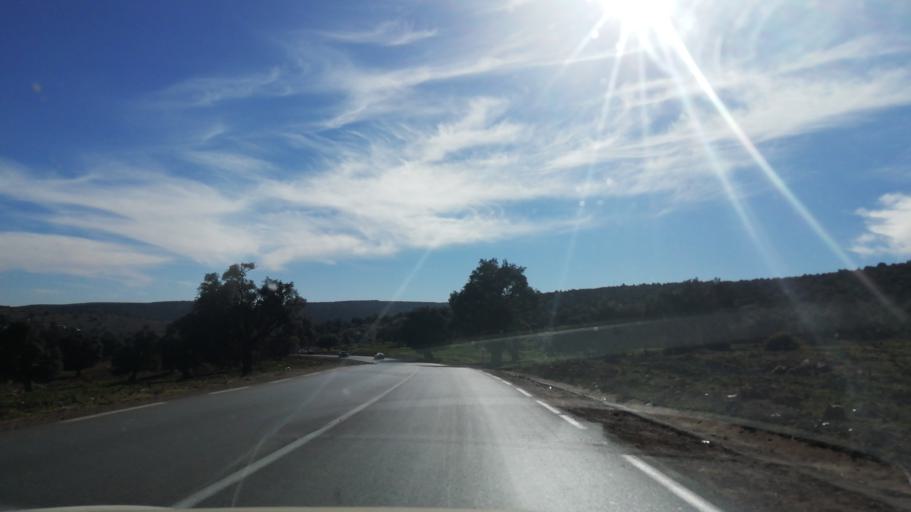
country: DZ
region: Tlemcen
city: Sebdou
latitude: 34.7349
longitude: -1.3388
